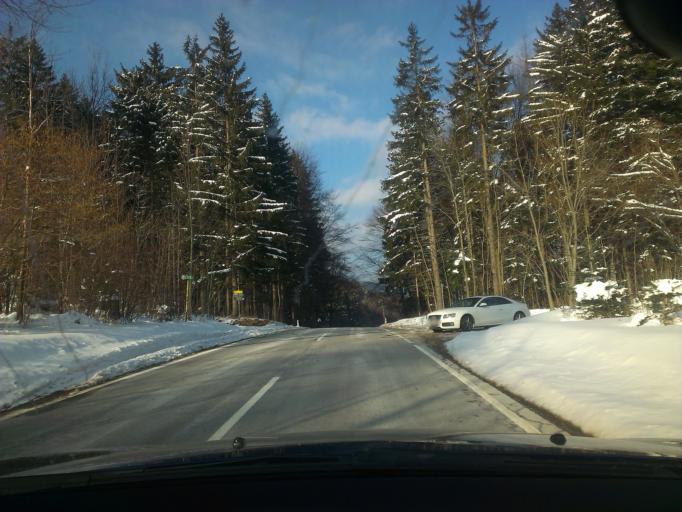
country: AT
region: Lower Austria
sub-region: Politischer Bezirk Neunkirchen
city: Puchberg am Schneeberg
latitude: 47.8140
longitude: 15.9411
